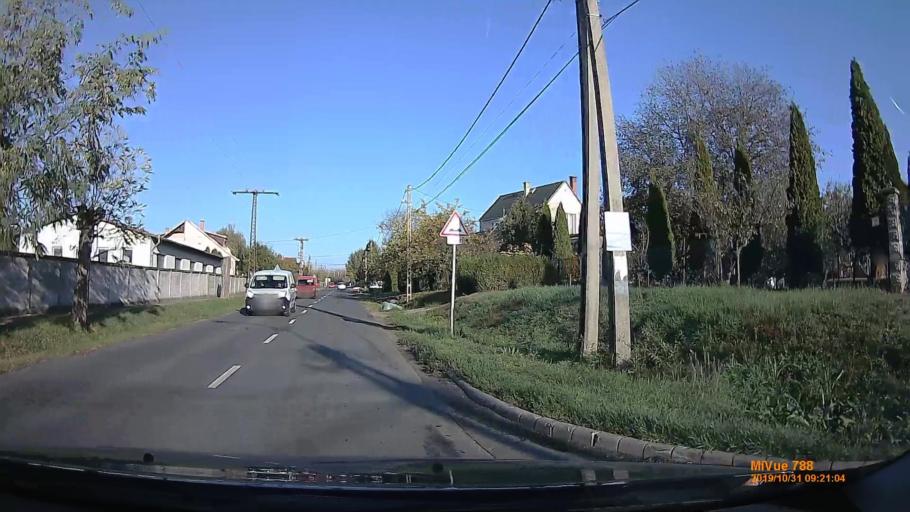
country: HU
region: Pest
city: Gyomro
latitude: 47.4283
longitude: 19.3827
